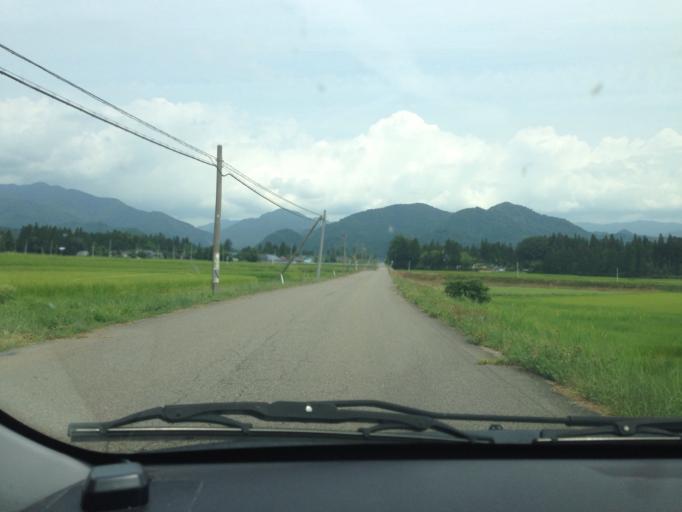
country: JP
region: Fukushima
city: Kitakata
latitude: 37.7147
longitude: 139.8587
